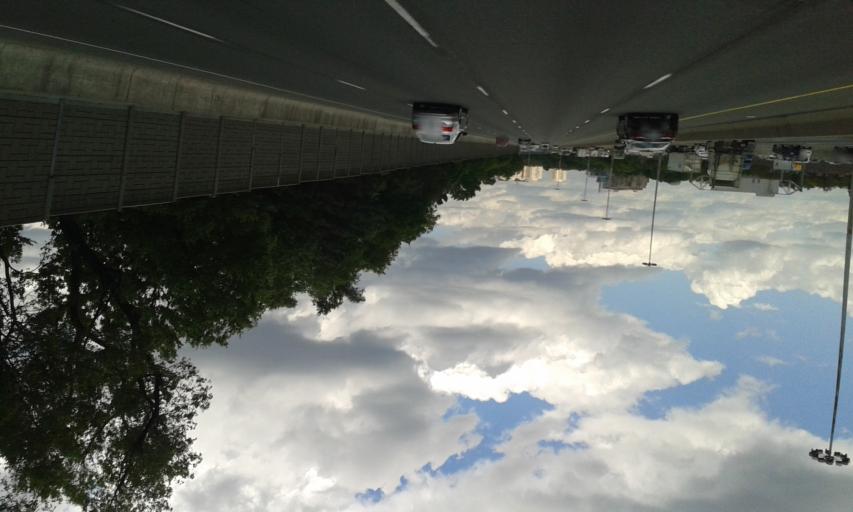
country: CA
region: Ontario
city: Willowdale
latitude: 43.7558
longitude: -79.4039
